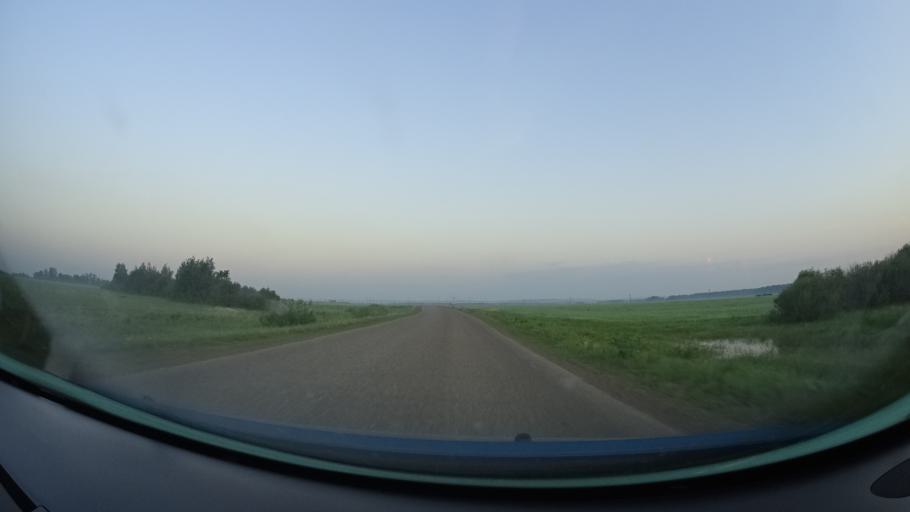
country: RU
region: Bashkortostan
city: Starobaltachevo
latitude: 56.0376
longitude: 55.9369
